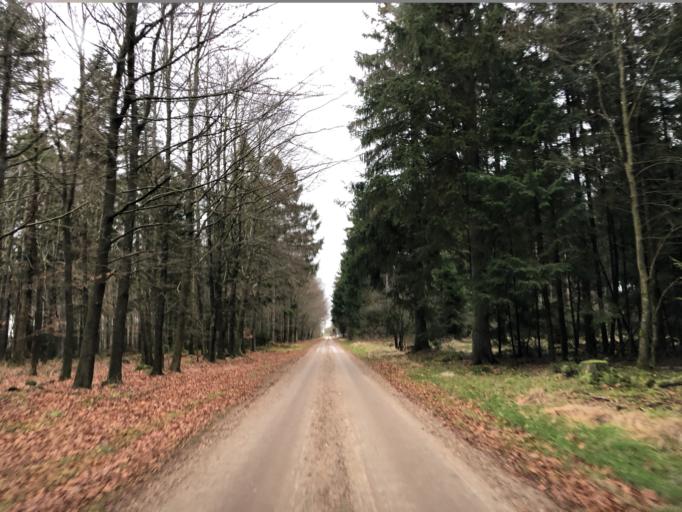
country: DK
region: Central Jutland
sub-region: Holstebro Kommune
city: Vinderup
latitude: 56.3919
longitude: 8.8692
